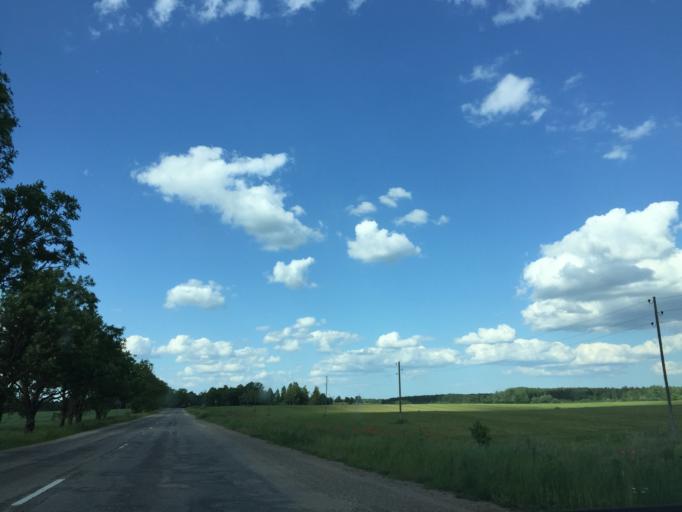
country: LV
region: Jaunpils
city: Jaunpils
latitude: 56.8441
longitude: 23.0416
